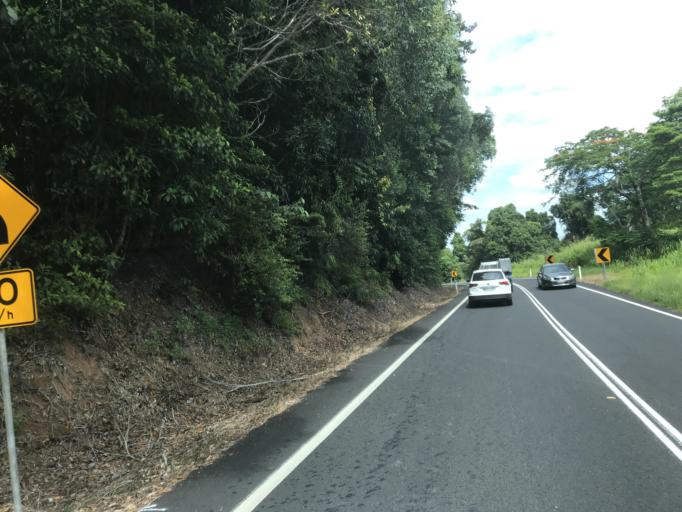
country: AU
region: Queensland
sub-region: Cassowary Coast
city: Innisfail
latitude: -17.8684
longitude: 146.0714
